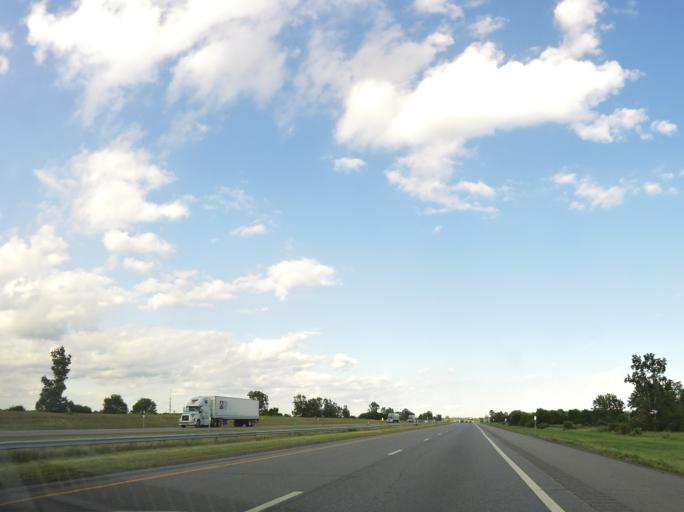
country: US
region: New York
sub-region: Erie County
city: Harris Hill
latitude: 42.9472
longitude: -78.6687
